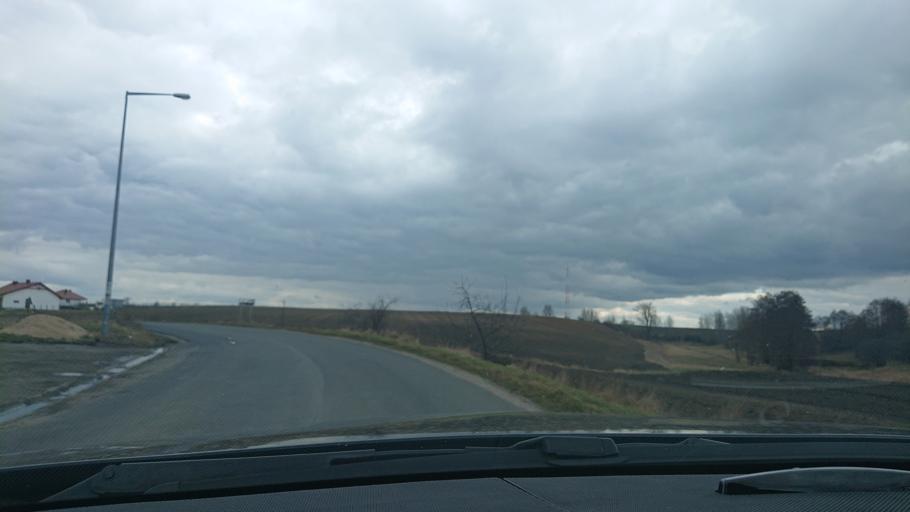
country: PL
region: Greater Poland Voivodeship
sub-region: Powiat gnieznienski
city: Gniezno
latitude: 52.5767
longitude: 17.6688
